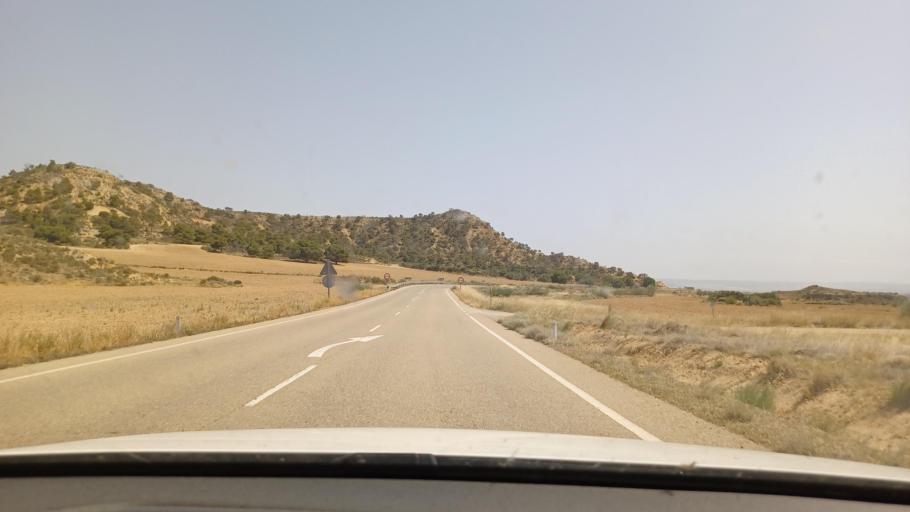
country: ES
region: Aragon
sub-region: Provincia de Zaragoza
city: Chiprana
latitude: 41.3381
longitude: -0.0894
